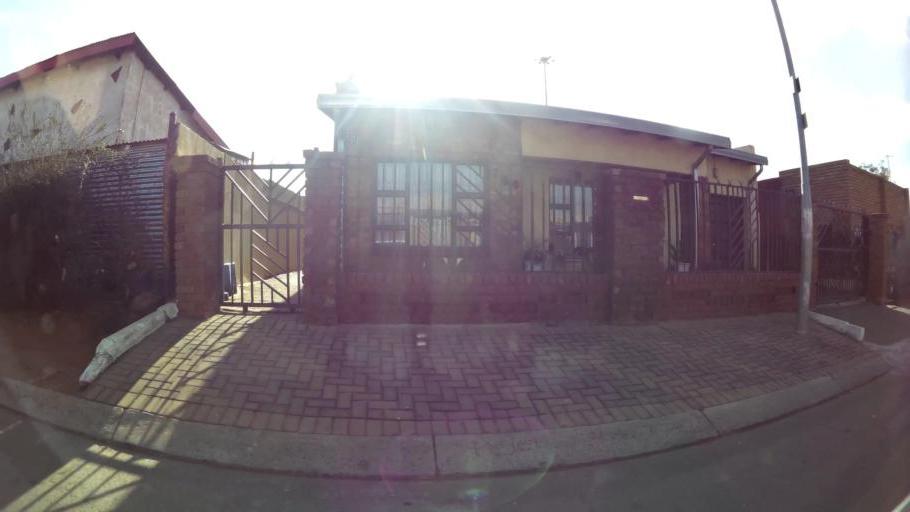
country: ZA
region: Gauteng
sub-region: City of Johannesburg Metropolitan Municipality
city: Soweto
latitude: -26.2541
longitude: 27.9151
